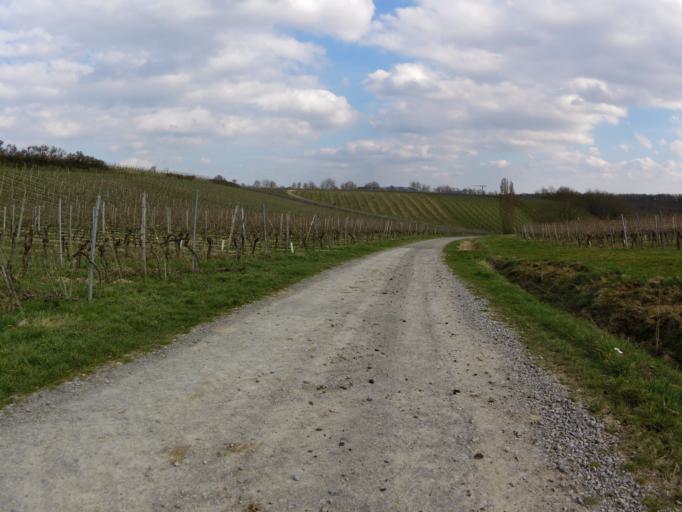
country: DE
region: Bavaria
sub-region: Regierungsbezirk Unterfranken
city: Buchbrunn
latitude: 49.7379
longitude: 10.1190
